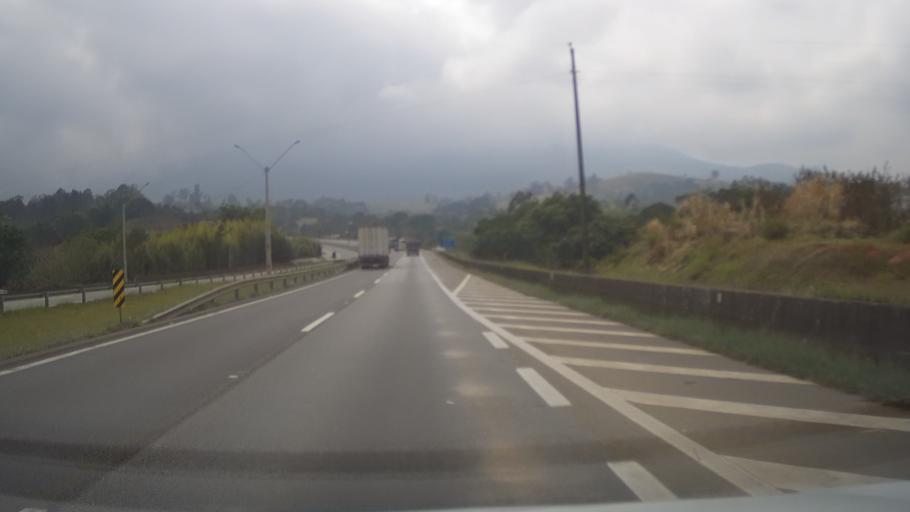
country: BR
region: Minas Gerais
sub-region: Extrema
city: Extrema
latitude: -22.8807
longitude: -46.3931
